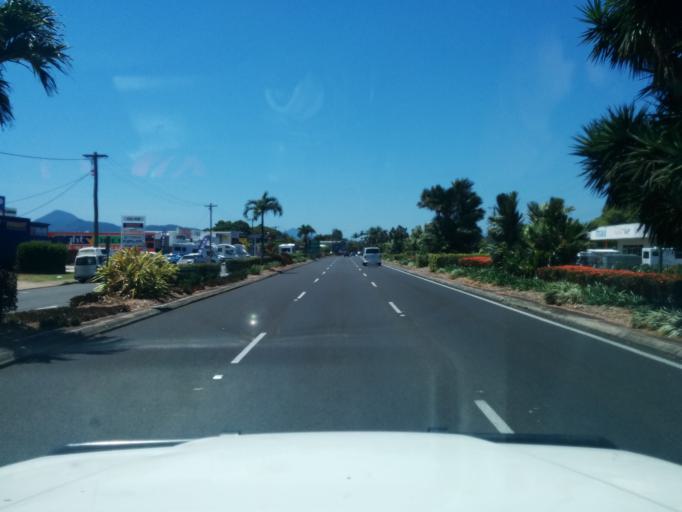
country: AU
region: Queensland
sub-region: Cairns
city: Cairns
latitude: -16.8949
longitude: 145.7541
